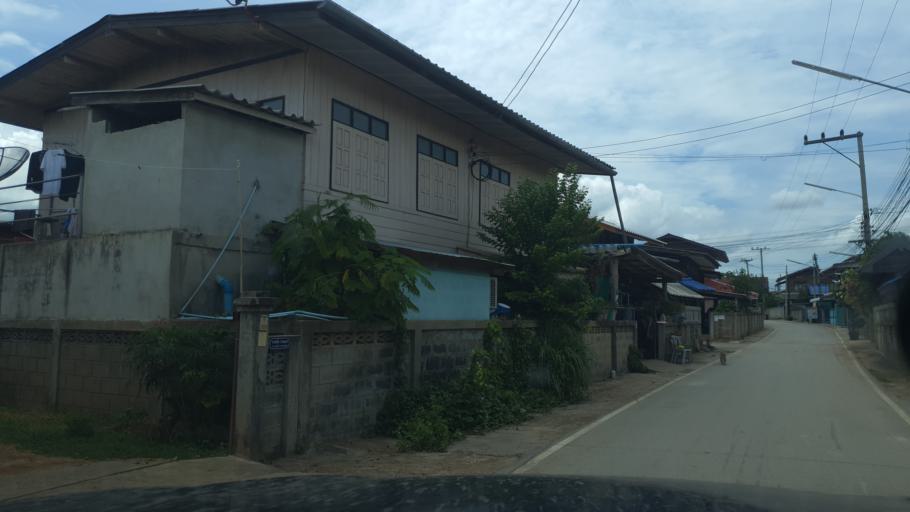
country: TH
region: Lampang
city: Sop Prap
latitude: 17.8810
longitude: 99.3830
